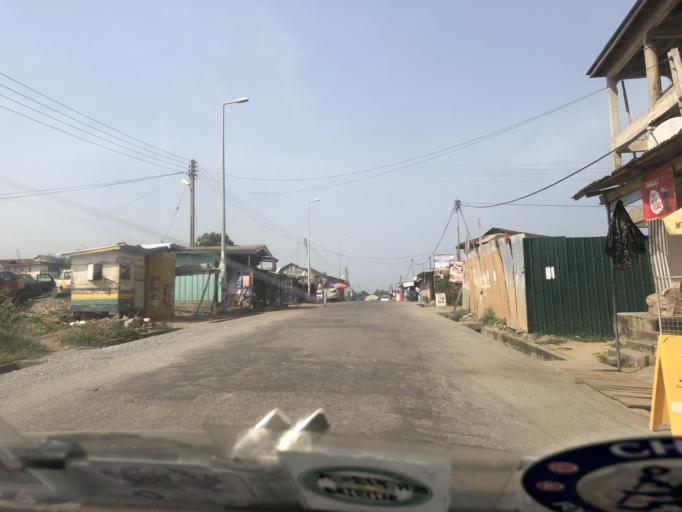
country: GH
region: Eastern
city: Koforidua
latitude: 6.0948
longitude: -0.2618
